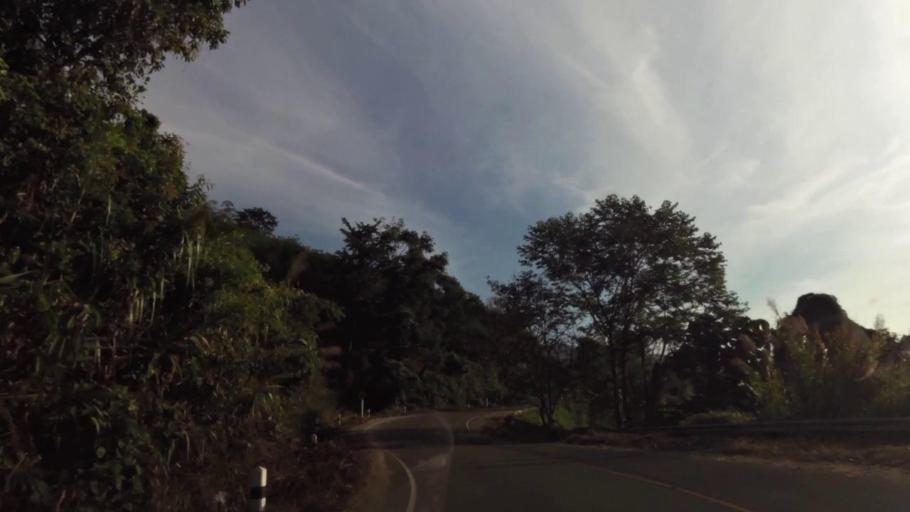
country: TH
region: Chiang Rai
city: Khun Tan
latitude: 19.8648
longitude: 100.4180
